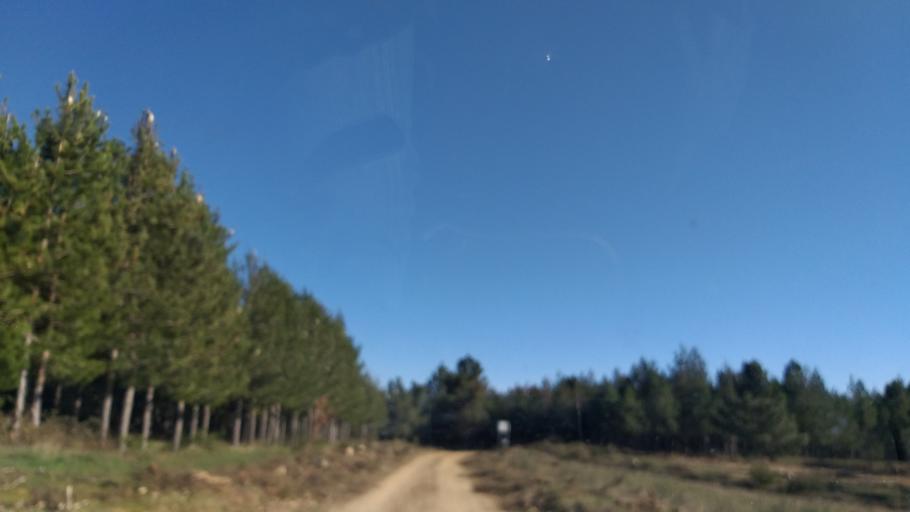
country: PT
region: Guarda
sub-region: Celorico da Beira
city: Celorico da Beira
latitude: 40.5154
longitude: -7.4096
